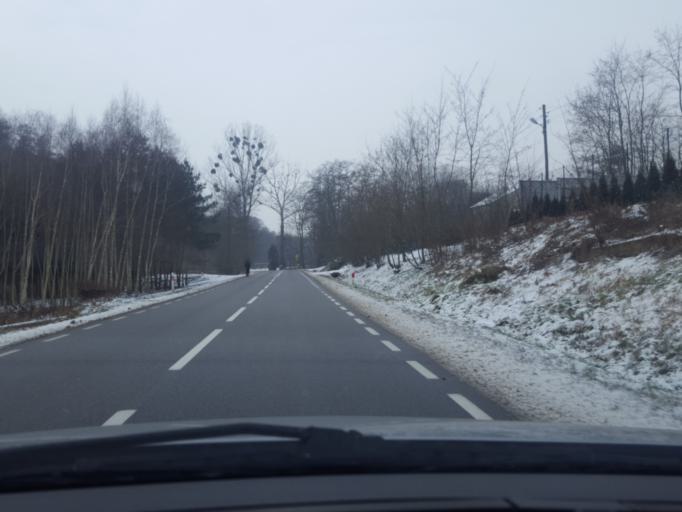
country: PL
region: Lodz Voivodeship
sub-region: Powiat brzezinski
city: Rogow
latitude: 51.8670
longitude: 19.8341
